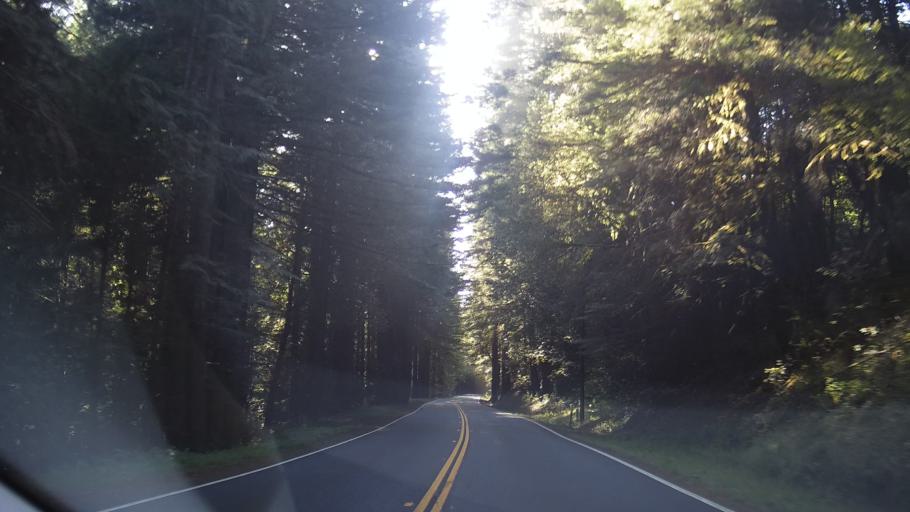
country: US
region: California
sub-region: Mendocino County
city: Fort Bragg
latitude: 39.3465
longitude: -123.5968
